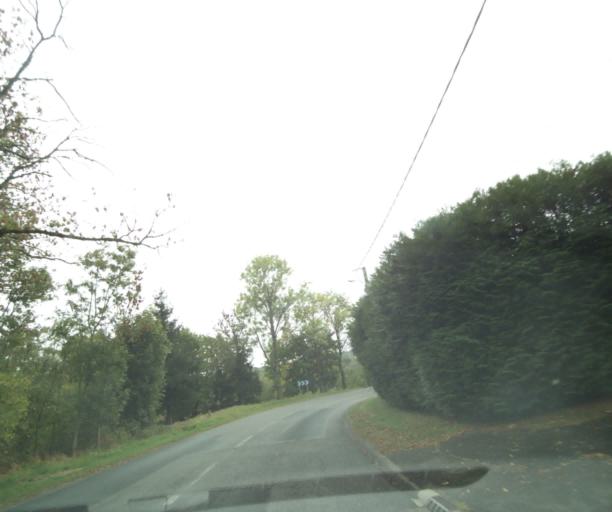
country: FR
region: Auvergne
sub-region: Departement du Puy-de-Dome
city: Orcines
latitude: 45.7709
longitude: 3.0101
